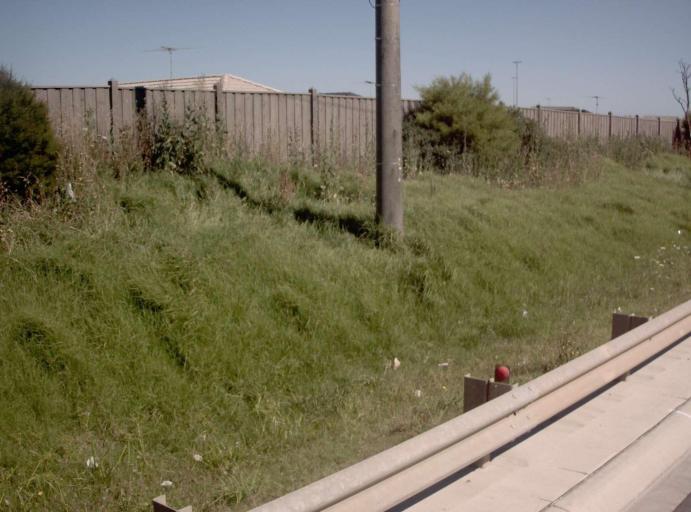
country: AU
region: Victoria
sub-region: Cardinia
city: Officer
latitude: -38.0643
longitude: 145.4372
